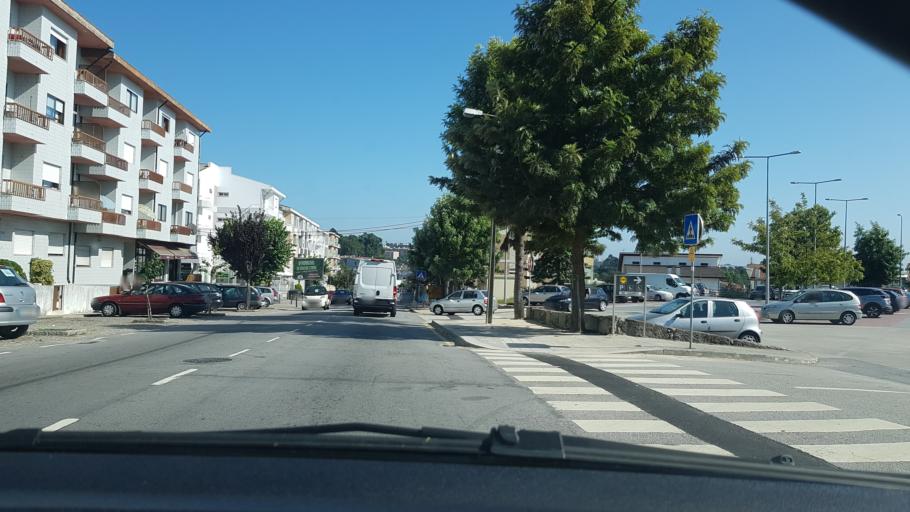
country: PT
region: Porto
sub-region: Gondomar
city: Baguim do Monte
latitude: 41.1828
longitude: -8.5375
